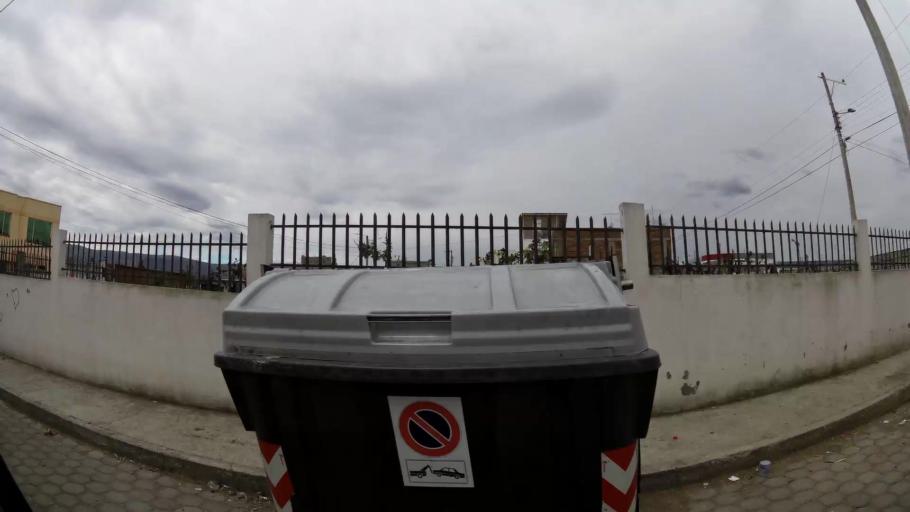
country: EC
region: Cotopaxi
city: Latacunga
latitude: -0.9542
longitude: -78.6036
